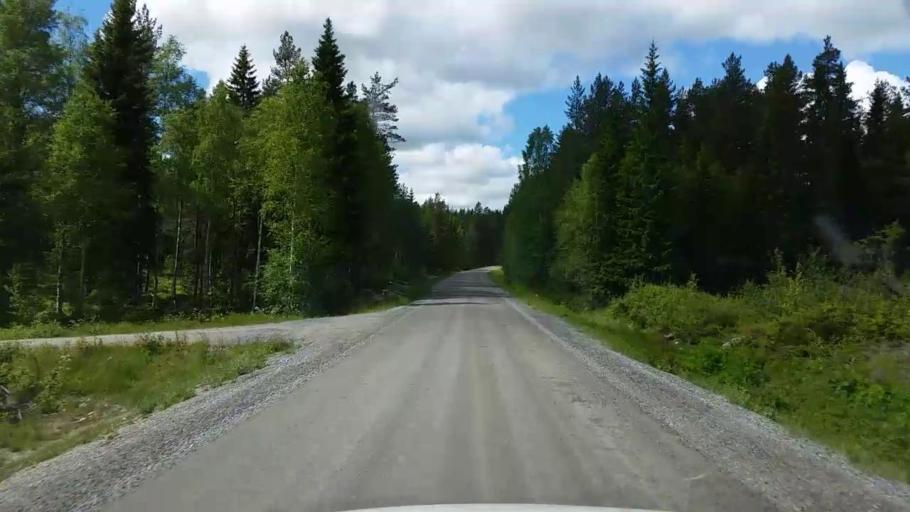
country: SE
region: Gaevleborg
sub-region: Bollnas Kommun
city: Vittsjo
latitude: 61.0915
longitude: 16.1764
